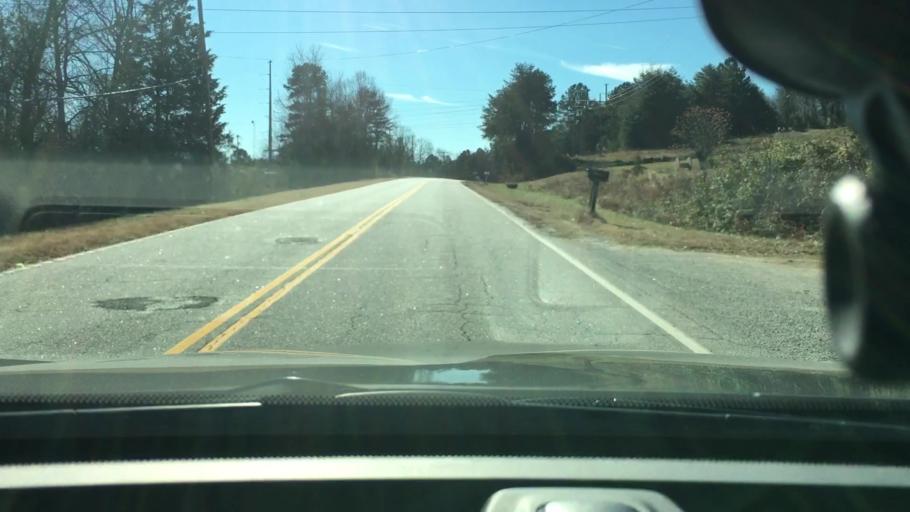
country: US
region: South Carolina
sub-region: Cherokee County
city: Gaffney
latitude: 35.0360
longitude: -81.6785
